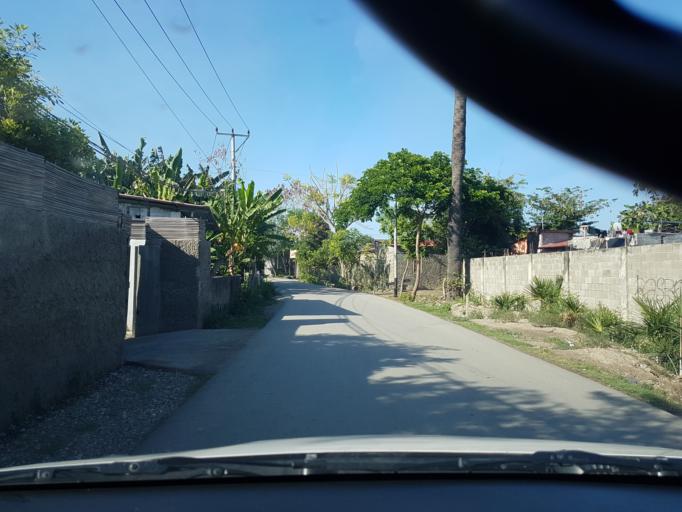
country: TL
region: Dili
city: Dili
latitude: -8.5420
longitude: 125.5421
